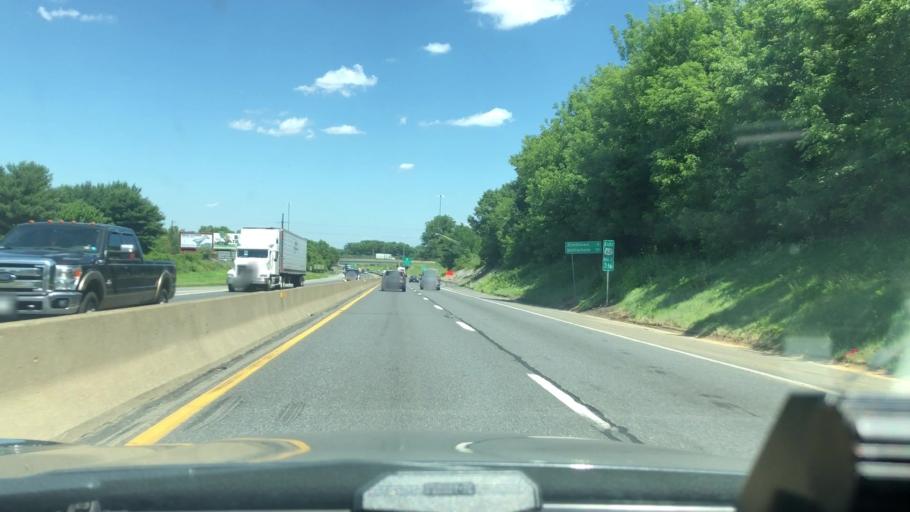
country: US
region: Pennsylvania
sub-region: Lehigh County
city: Wescosville
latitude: 40.5942
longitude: -75.5778
